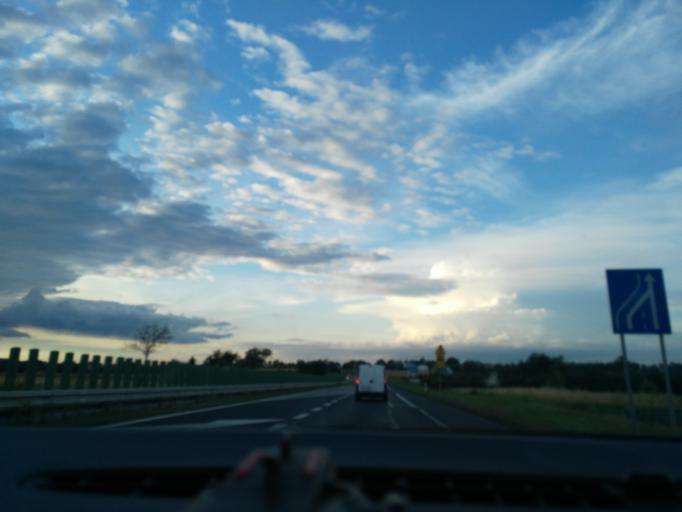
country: PL
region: Lublin Voivodeship
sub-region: Powiat lubelski
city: Niemce
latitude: 51.3400
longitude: 22.6185
